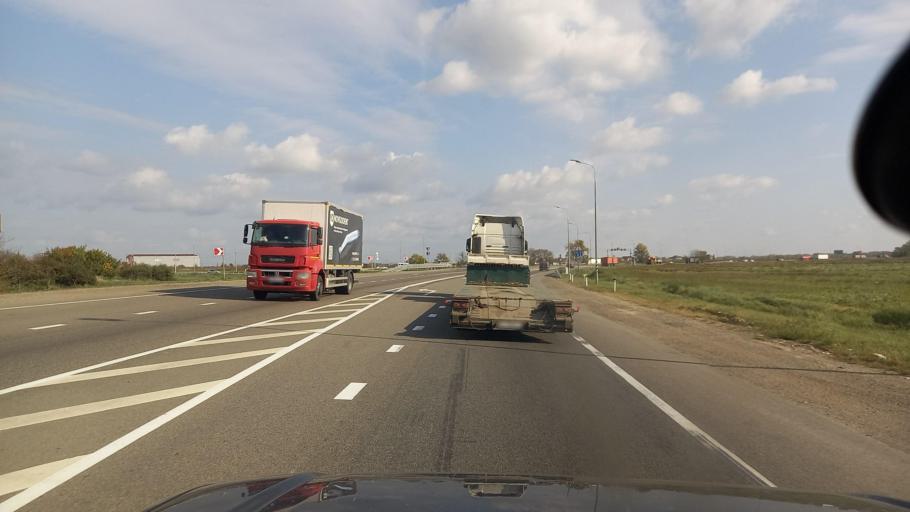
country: RU
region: Krasnodarskiy
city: Abinsk
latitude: 44.8574
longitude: 38.1894
